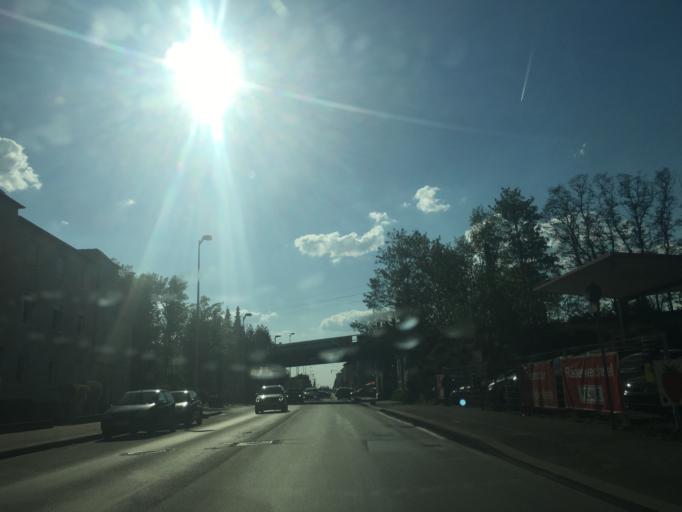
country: DE
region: North Rhine-Westphalia
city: Haan
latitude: 51.1676
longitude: 6.9947
